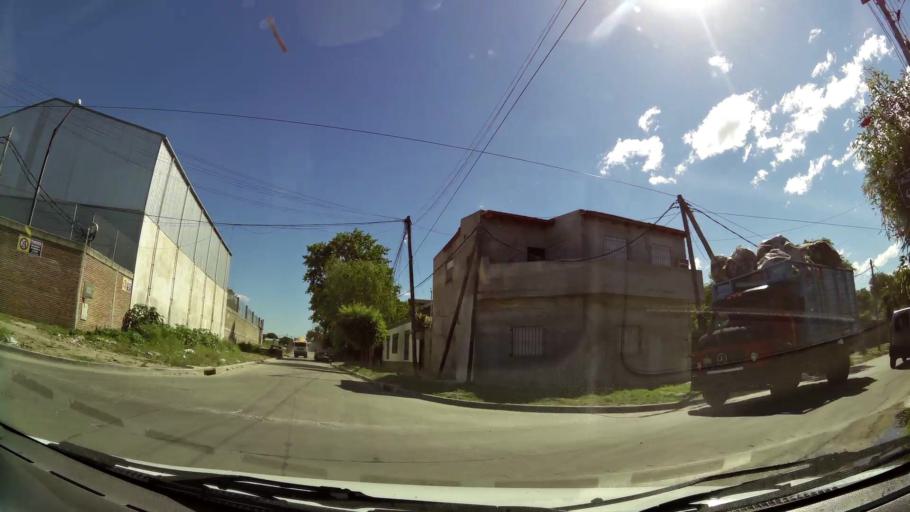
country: AR
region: Buenos Aires
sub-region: Partido de General San Martin
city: General San Martin
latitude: -34.5204
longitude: -58.5766
